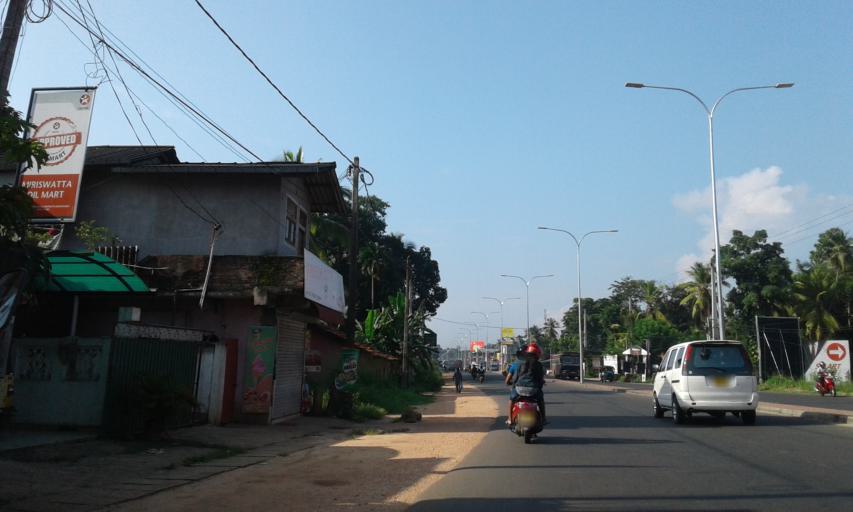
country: LK
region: Western
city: Gampaha
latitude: 7.0718
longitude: 80.0146
